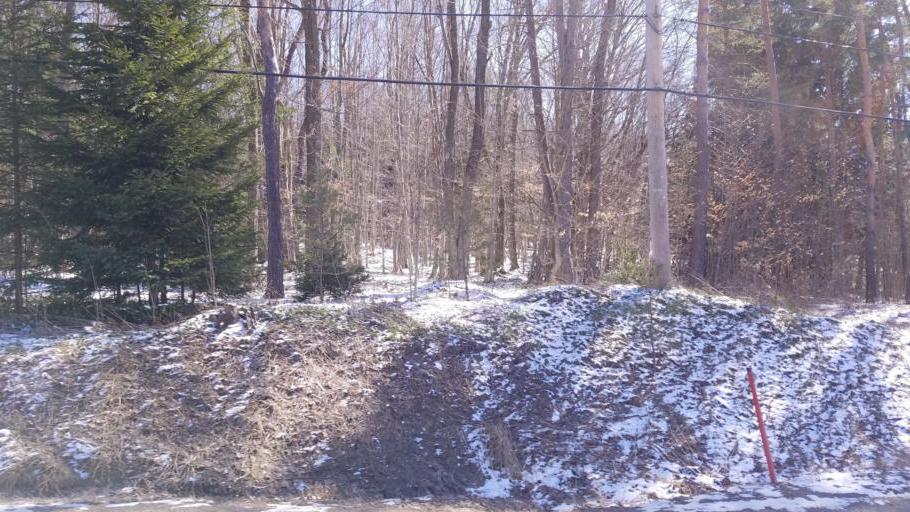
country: US
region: Pennsylvania
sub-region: Potter County
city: Galeton
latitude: 41.9104
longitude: -77.7577
